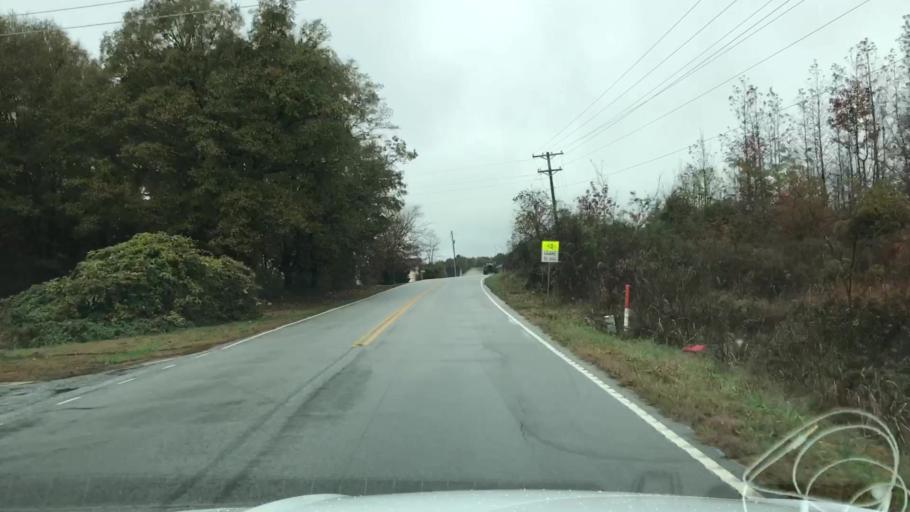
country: US
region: South Carolina
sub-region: Spartanburg County
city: Roebuck
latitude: 34.7959
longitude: -81.9149
